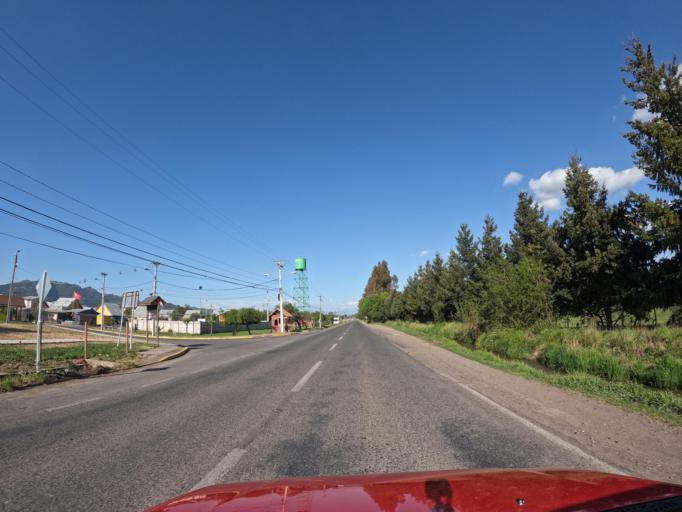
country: CL
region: Maule
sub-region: Provincia de Curico
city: Rauco
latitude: -34.8684
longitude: -71.2602
